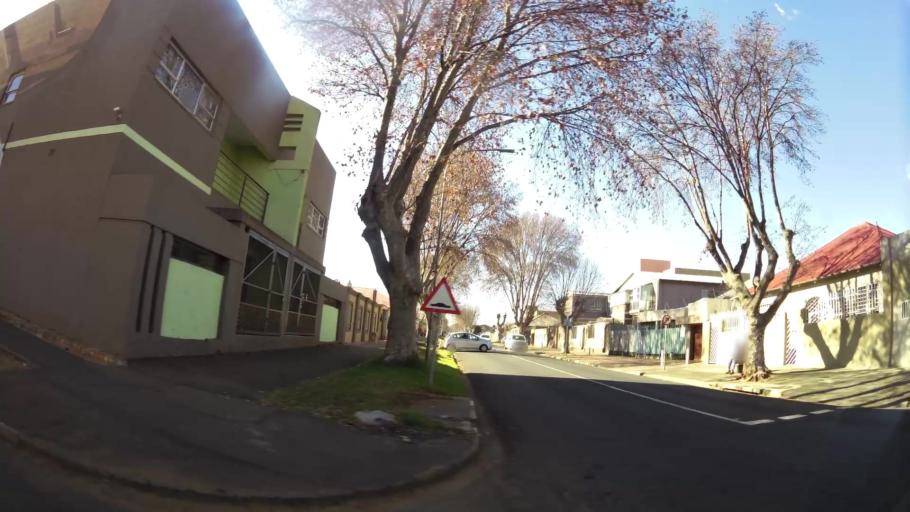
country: ZA
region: Gauteng
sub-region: City of Johannesburg Metropolitan Municipality
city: Johannesburg
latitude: -26.1991
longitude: 28.0063
